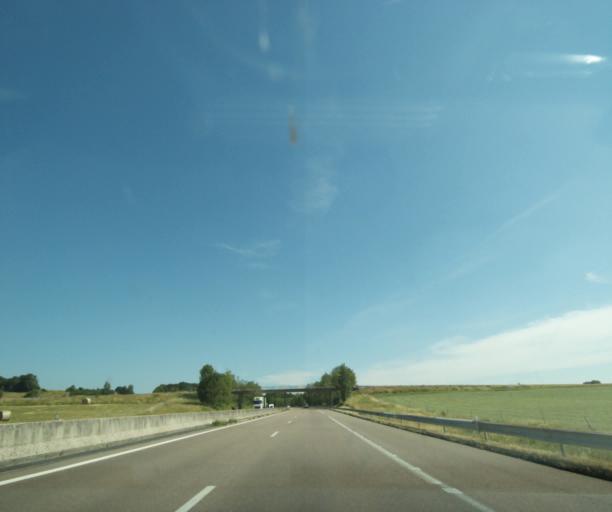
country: FR
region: Lorraine
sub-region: Departement des Vosges
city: Chatenois
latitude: 48.3958
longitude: 5.8806
